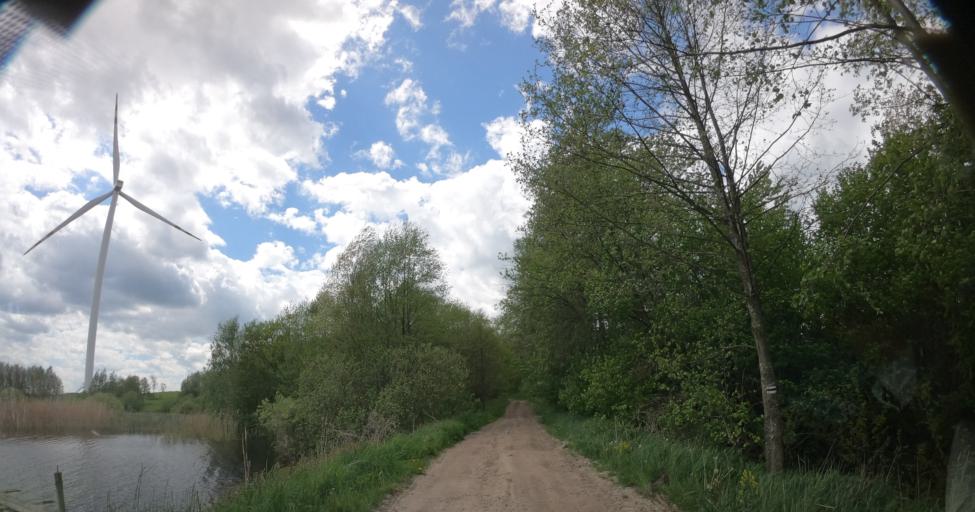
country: PL
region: West Pomeranian Voivodeship
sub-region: Powiat drawski
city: Drawsko Pomorskie
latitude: 53.5626
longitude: 15.7760
